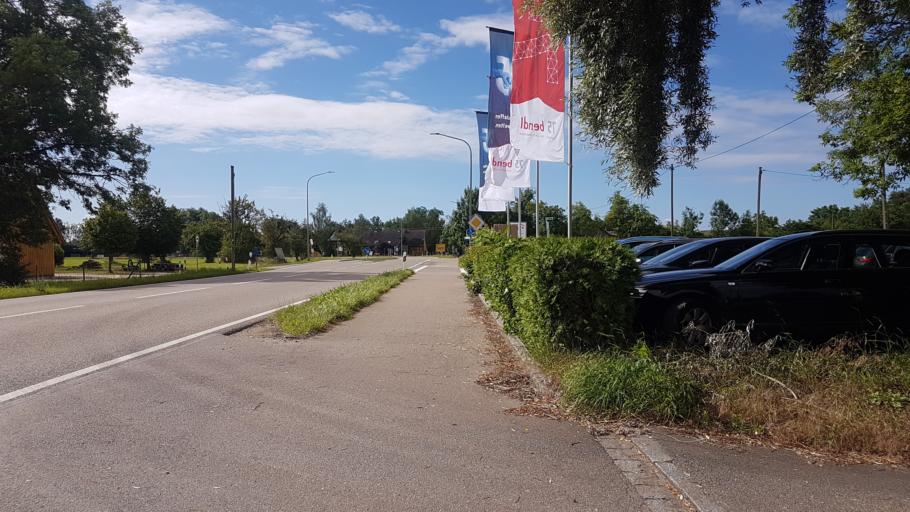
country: DE
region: Bavaria
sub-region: Swabia
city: Guenzburg
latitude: 48.4793
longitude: 10.2601
